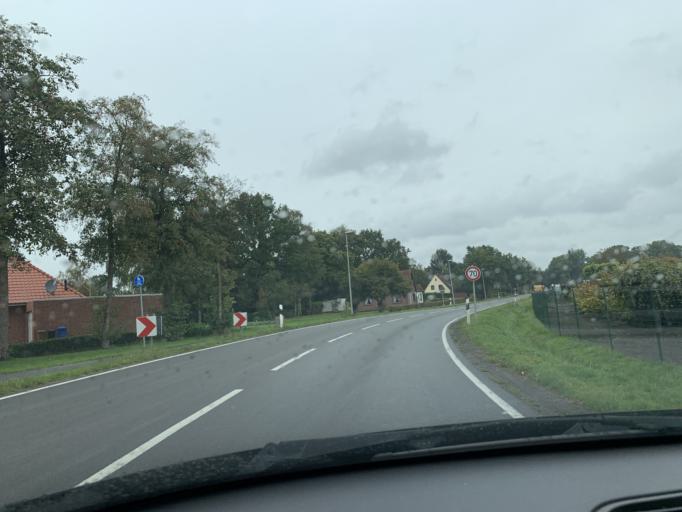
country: DE
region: Lower Saxony
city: Bad Zwischenahn
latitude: 53.1670
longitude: 8.0666
